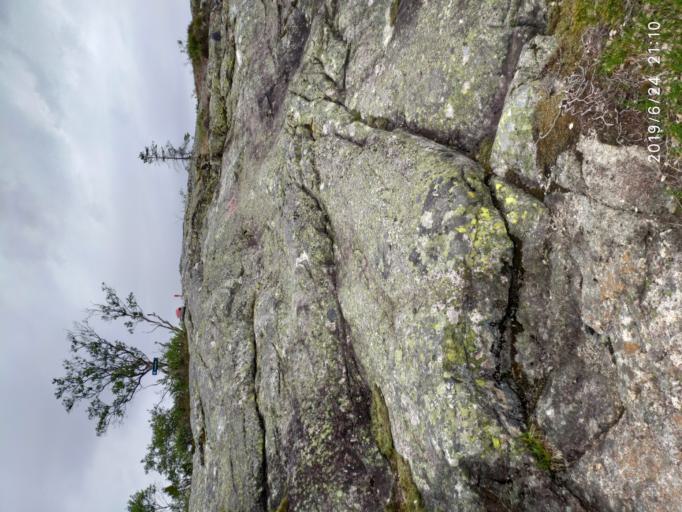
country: NO
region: Vest-Agder
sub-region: Sirdal
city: Tonstad
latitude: 58.7590
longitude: 6.7180
